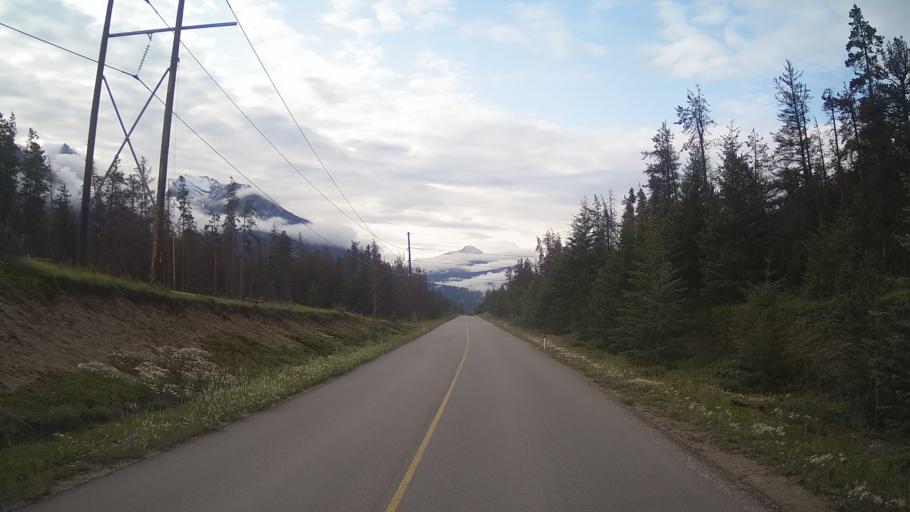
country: CA
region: Alberta
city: Jasper Park Lodge
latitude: 52.9883
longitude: -118.0819
